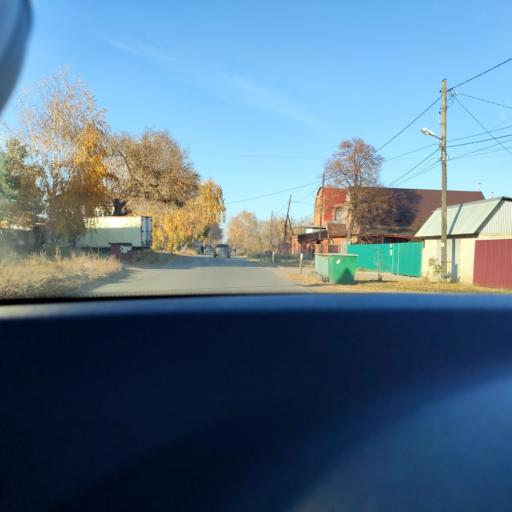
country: RU
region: Samara
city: Petra-Dubrava
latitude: 53.2547
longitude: 50.3291
